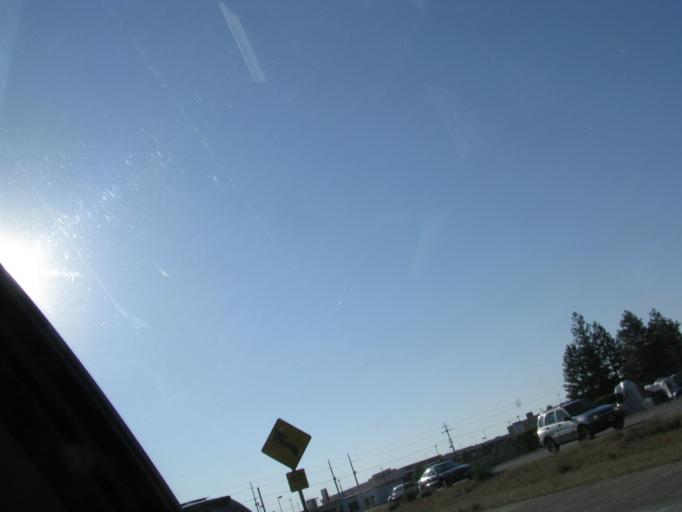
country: US
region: Washington
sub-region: Spokane County
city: Dishman
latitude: 47.6568
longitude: -117.3225
